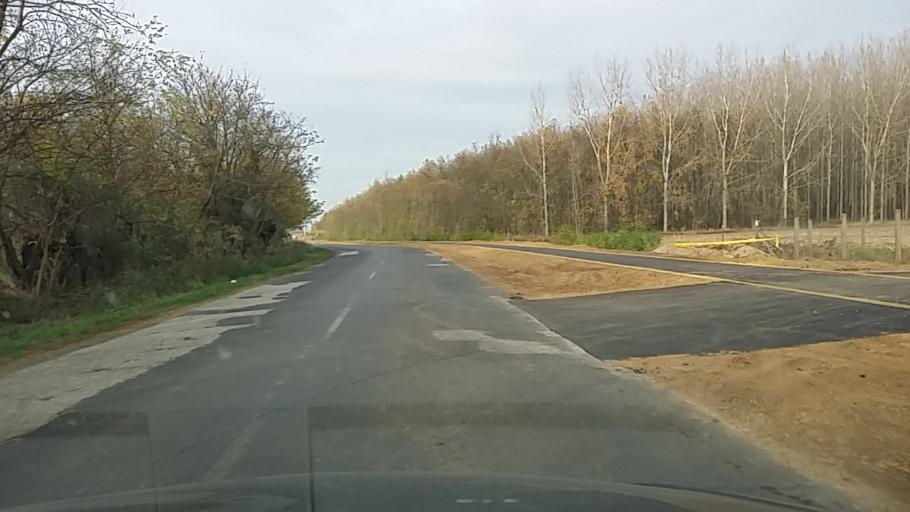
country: HU
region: Szabolcs-Szatmar-Bereg
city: Nyirbogdany
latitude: 48.0688
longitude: 21.8604
